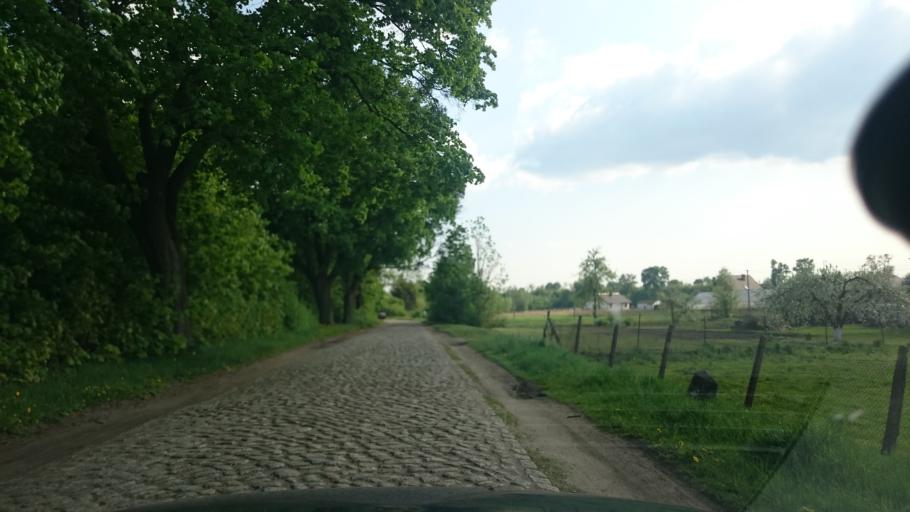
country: PL
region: Kujawsko-Pomorskie
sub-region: Grudziadz
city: Grudziadz
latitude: 53.4834
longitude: 18.8131
